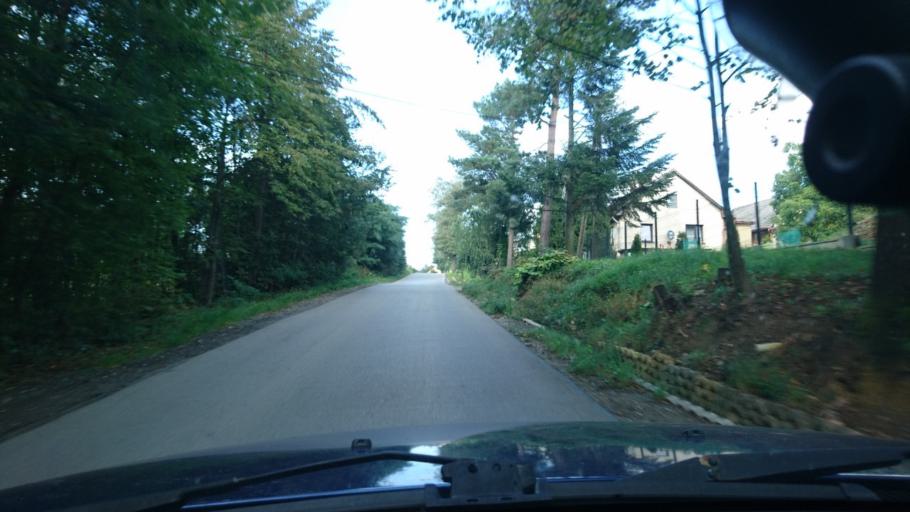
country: PL
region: Silesian Voivodeship
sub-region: Powiat bielski
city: Jasienica
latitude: 49.8236
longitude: 18.9272
